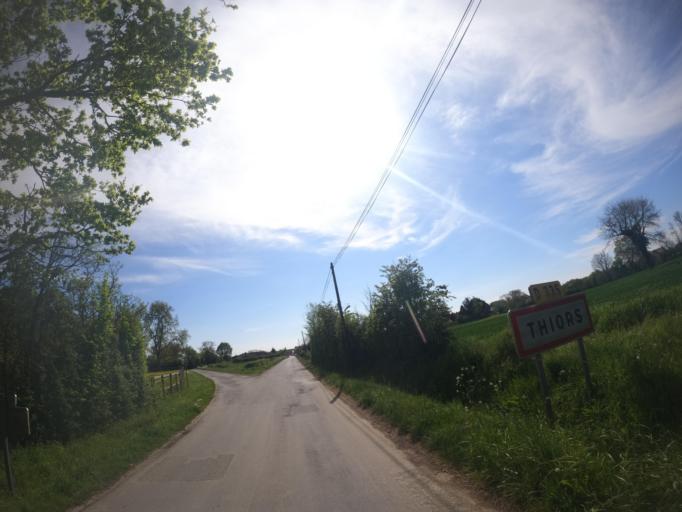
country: FR
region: Poitou-Charentes
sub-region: Departement des Deux-Sevres
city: Saint-Varent
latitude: 46.9263
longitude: -0.2194
